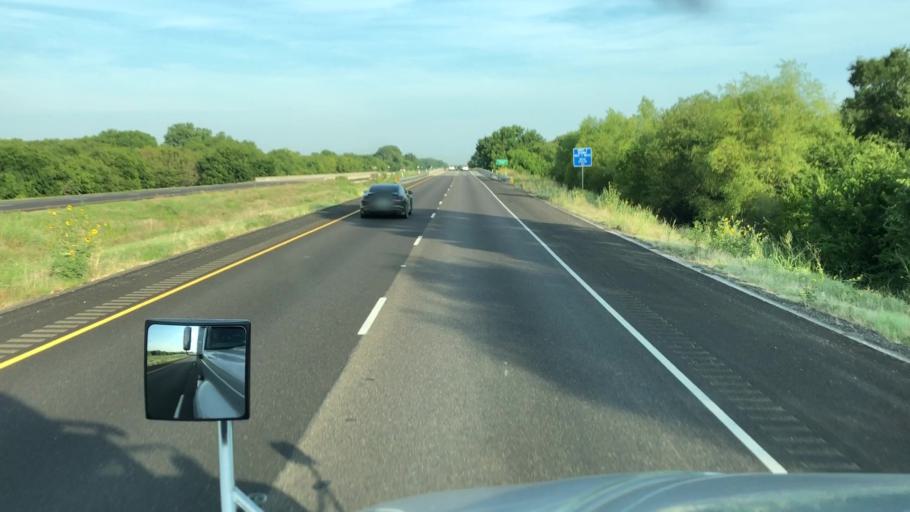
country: US
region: Texas
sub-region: McLennan County
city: Bellmead
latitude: 31.5356
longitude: -97.0303
